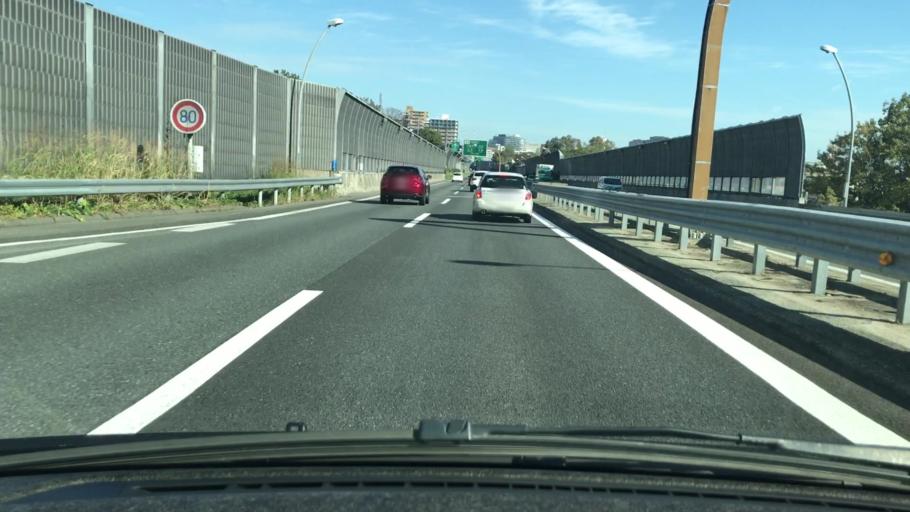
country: JP
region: Osaka
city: Suita
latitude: 34.7849
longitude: 135.5289
